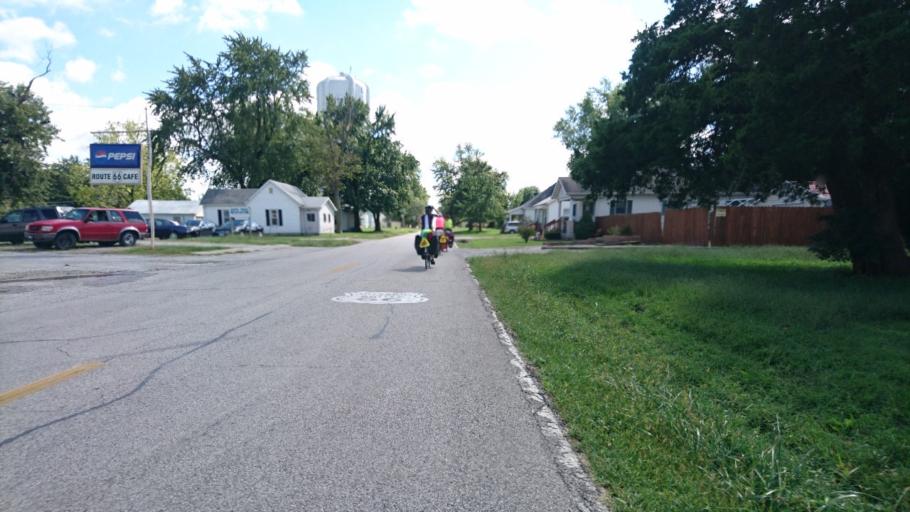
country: US
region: Illinois
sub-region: Montgomery County
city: Litchfield
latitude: 39.1733
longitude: -89.6668
